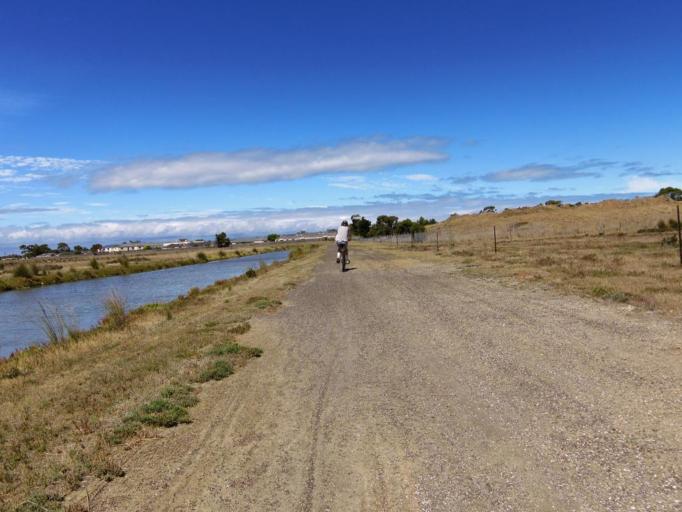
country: AU
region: Victoria
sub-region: Hobsons Bay
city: Altona Meadows
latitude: -37.8719
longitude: 144.7993
